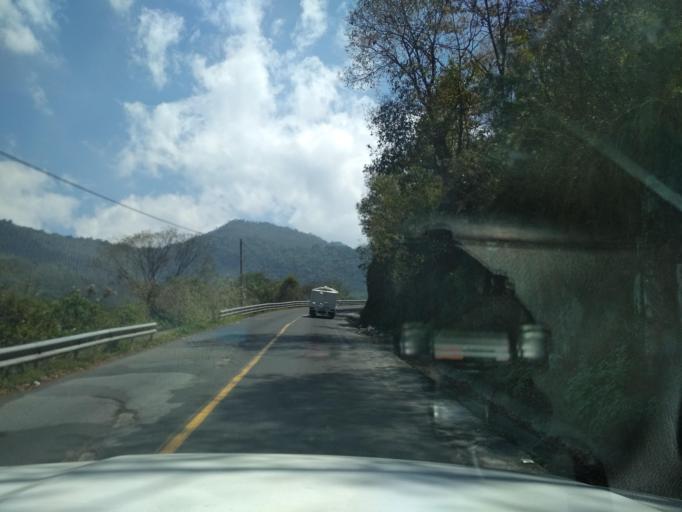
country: MX
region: Veracruz
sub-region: Tlilapan
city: Tonalixco
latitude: 18.7822
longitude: -97.0837
